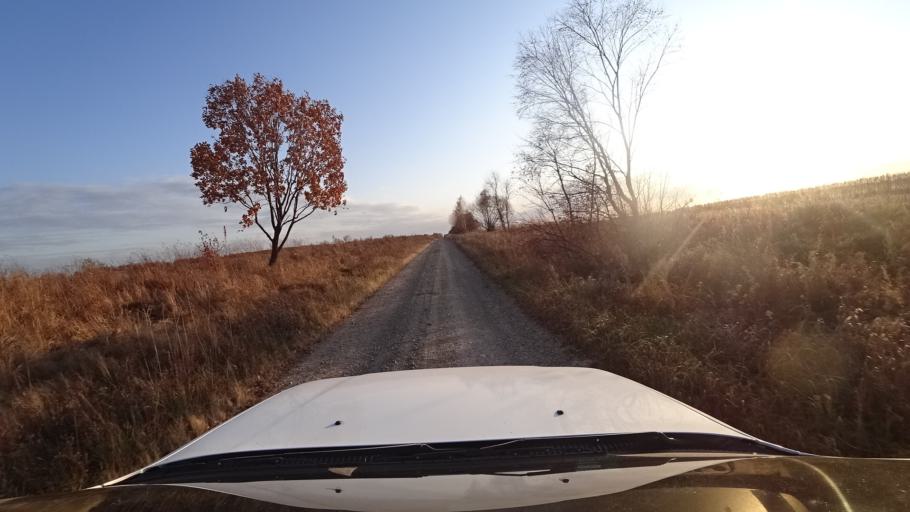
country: RU
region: Primorskiy
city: Lazo
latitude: 45.8129
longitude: 133.6093
